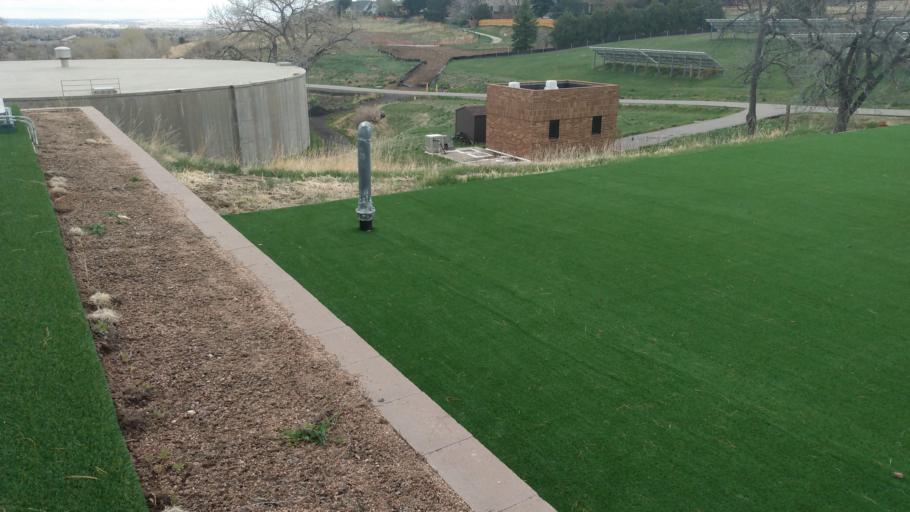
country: US
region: Colorado
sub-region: Boulder County
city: Louisville
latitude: 39.9911
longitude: -105.1534
